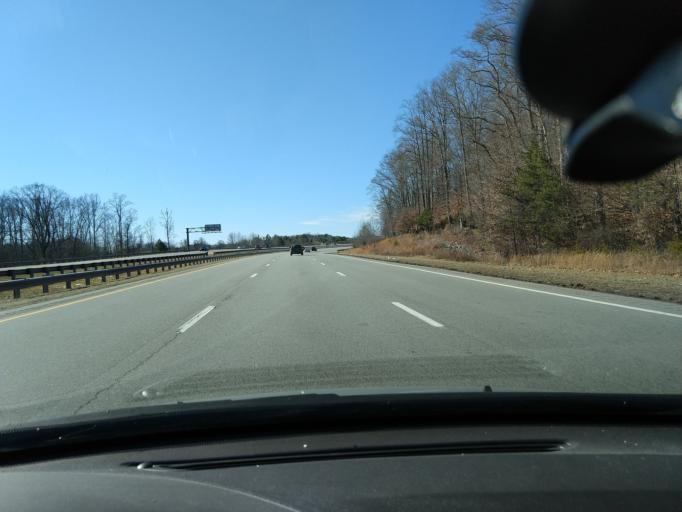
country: US
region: North Carolina
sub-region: Guilford County
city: Summerfield
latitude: 36.1163
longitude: -79.8987
